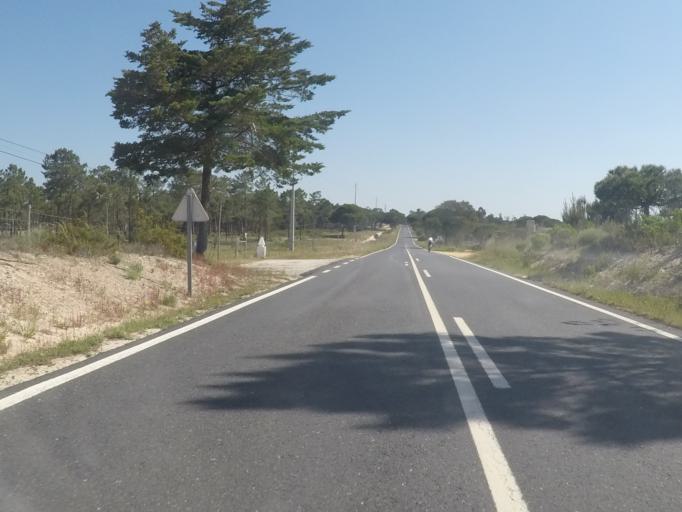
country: PT
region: Setubal
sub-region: Grandola
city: Grandola
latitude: 38.2571
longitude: -8.7362
